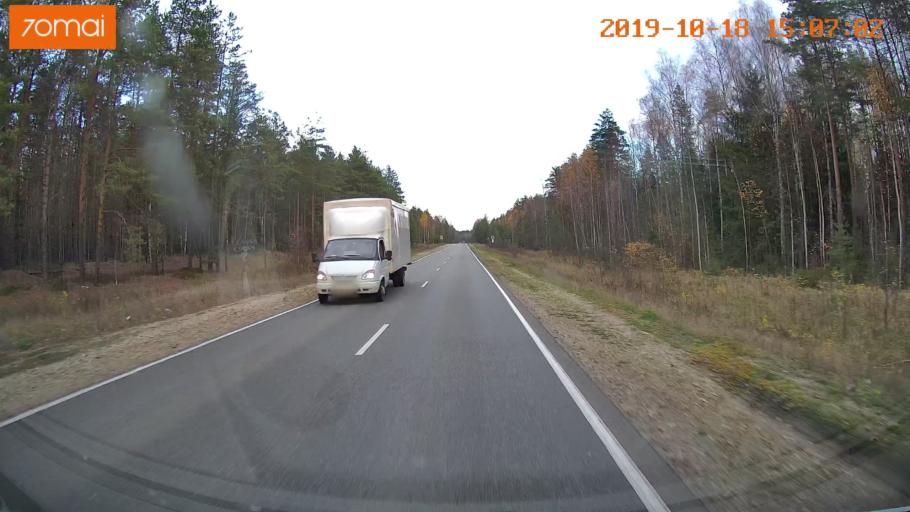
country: RU
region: Vladimir
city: Gus'-Khrustal'nyy
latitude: 55.5363
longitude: 40.5891
